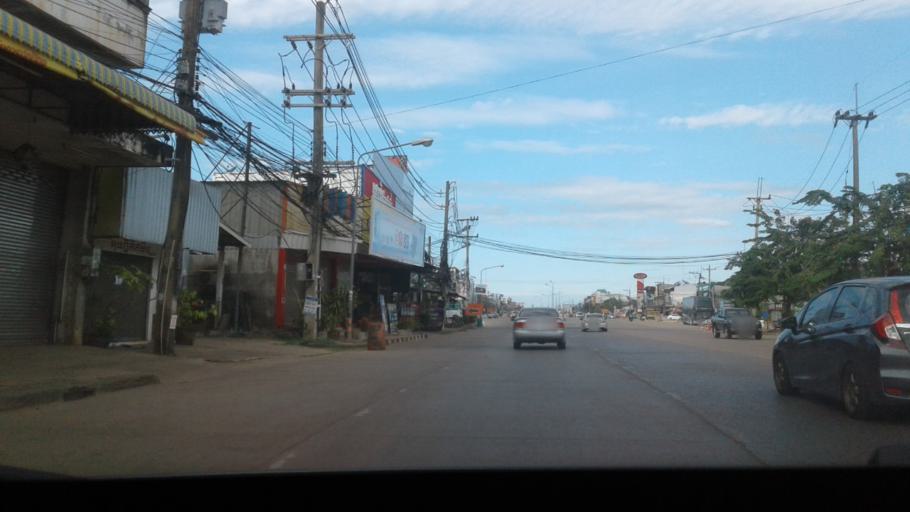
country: TH
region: Changwat Udon Thani
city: Udon Thani
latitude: 17.4277
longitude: 102.7909
